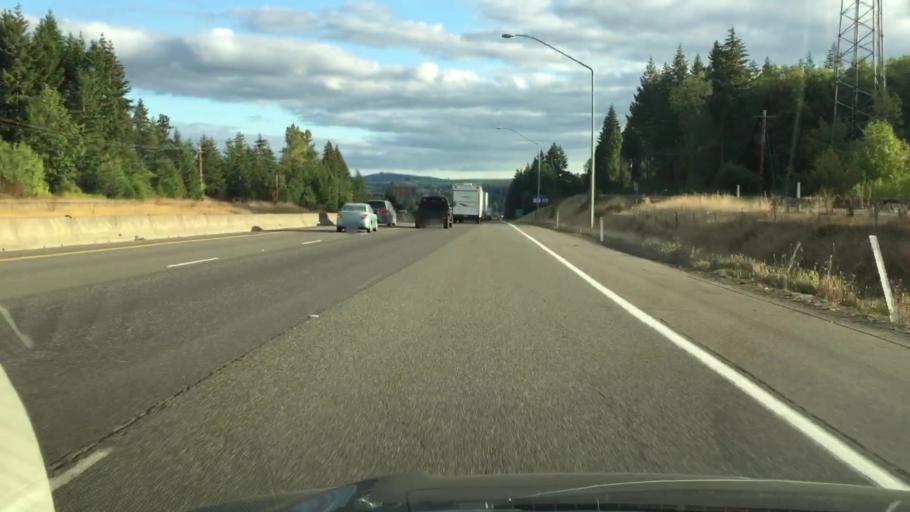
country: US
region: Washington
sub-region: Lewis County
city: Winlock
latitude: 46.4346
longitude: -122.8894
